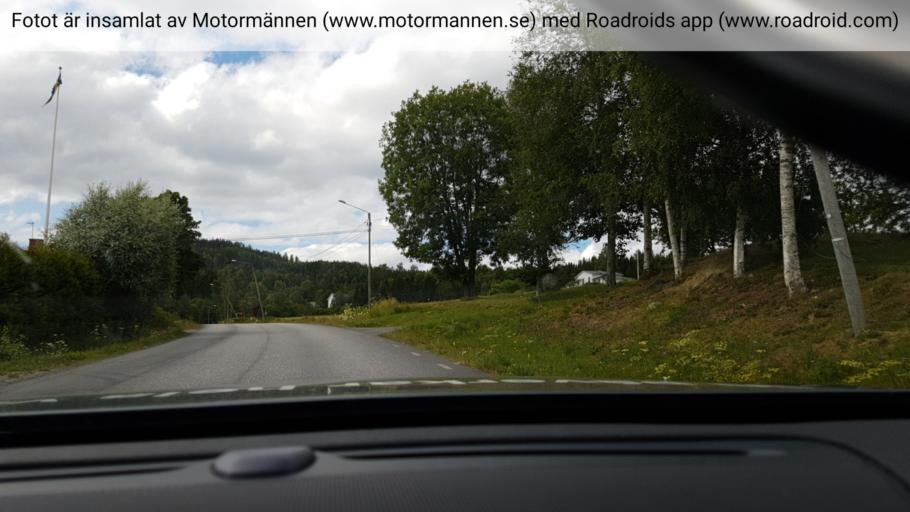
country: SE
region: Vaesternorrland
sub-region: Kramfors Kommun
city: Nordingra
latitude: 62.9378
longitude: 18.2395
